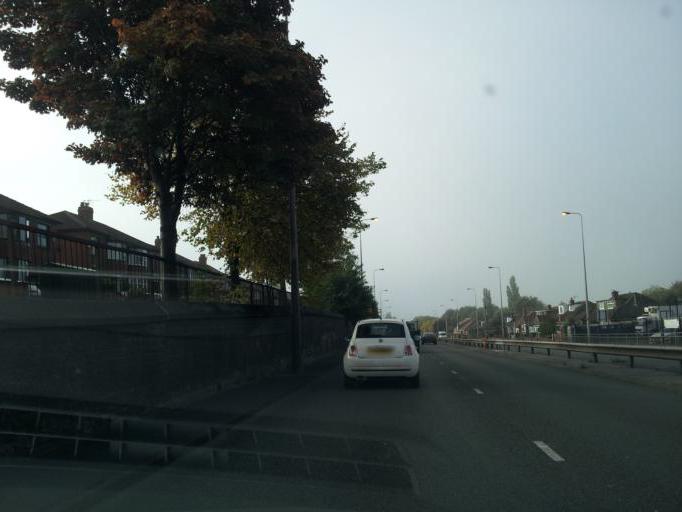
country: GB
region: England
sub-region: Borough of Oldham
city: Royton
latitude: 53.5529
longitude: -2.1416
